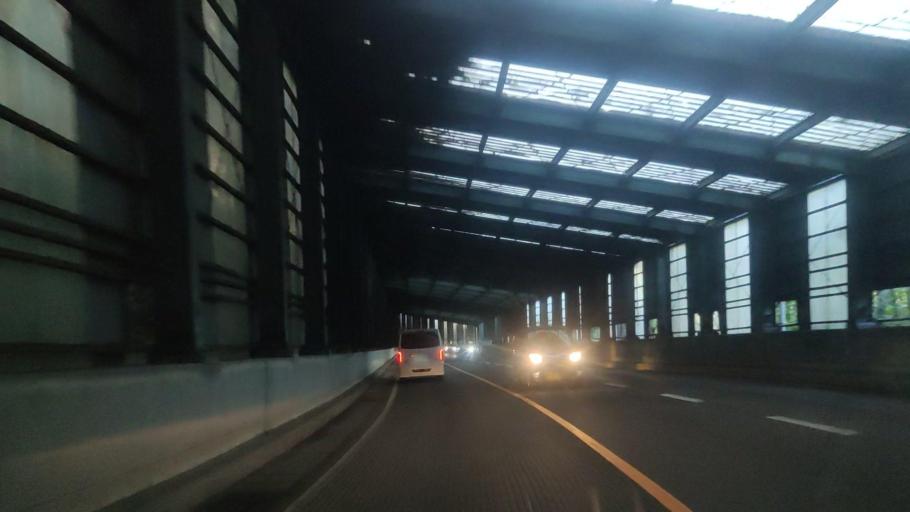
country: JP
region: Nagano
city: Kamimaruko
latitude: 36.1781
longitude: 138.2823
